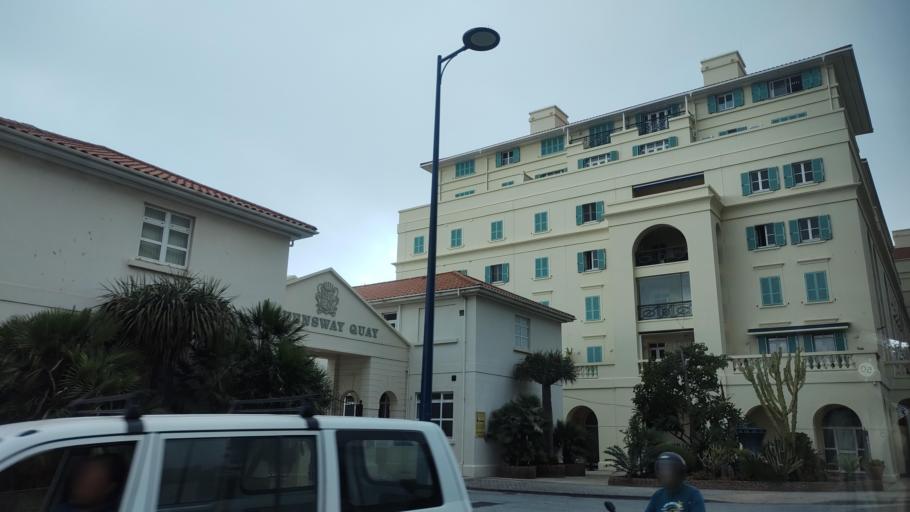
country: GI
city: Gibraltar
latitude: 36.1340
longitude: -5.3539
